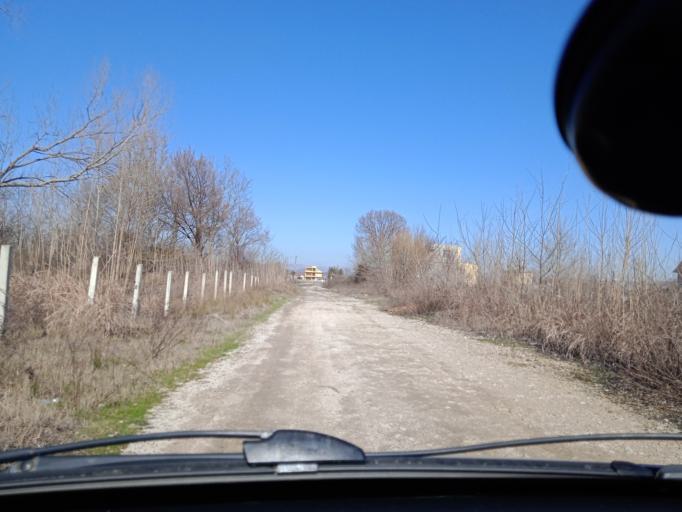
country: AL
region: Shkoder
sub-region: Rrethi i Shkodres
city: Velipoje
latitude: 41.8653
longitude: 19.4190
